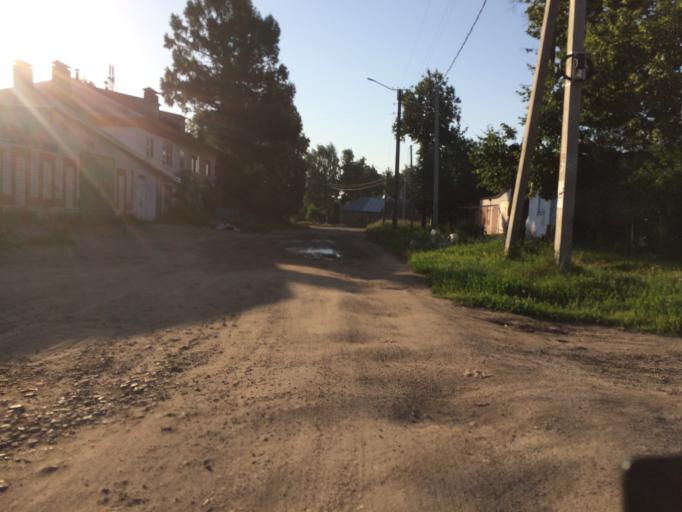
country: RU
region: Mariy-El
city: Yoshkar-Ola
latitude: 56.6509
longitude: 47.9045
